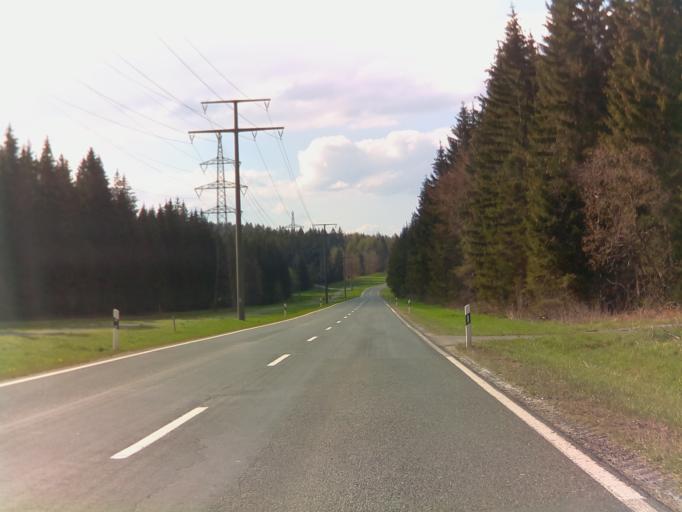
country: DE
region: Thuringia
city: Grafenthal
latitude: 50.4706
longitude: 11.3138
